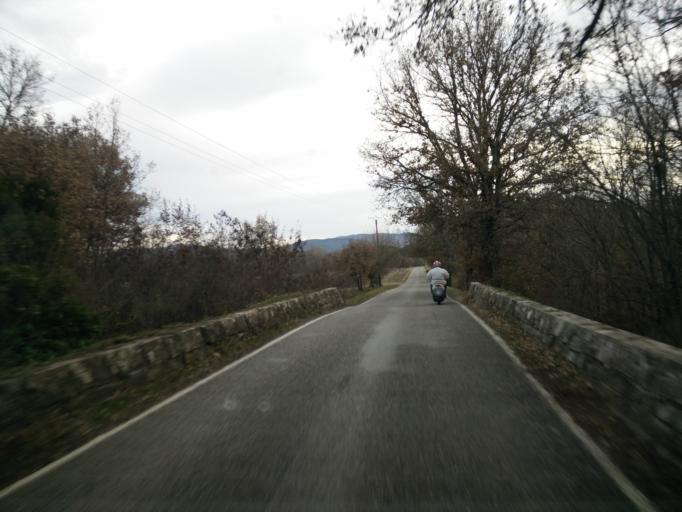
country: FR
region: Provence-Alpes-Cote d'Azur
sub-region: Departement du Var
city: Vidauban
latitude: 43.3875
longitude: 6.4418
